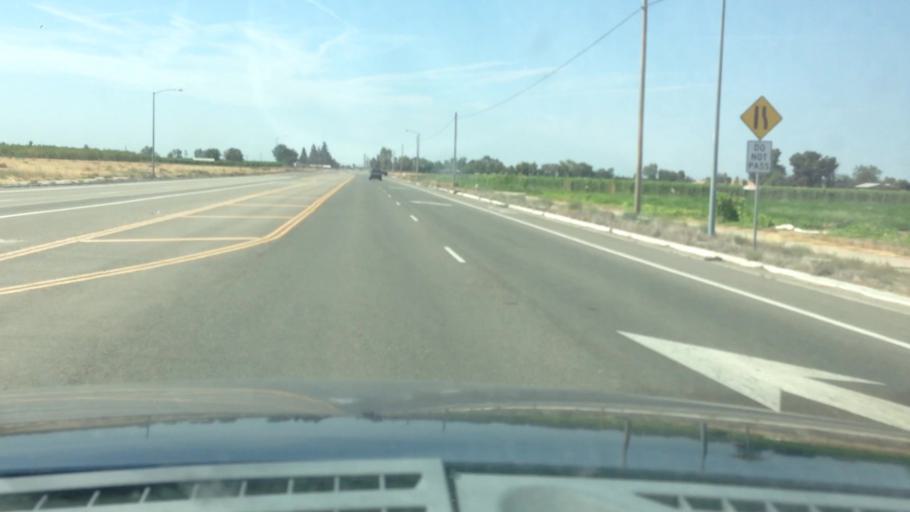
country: US
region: California
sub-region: Fresno County
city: Parlier
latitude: 36.6032
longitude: -119.5570
